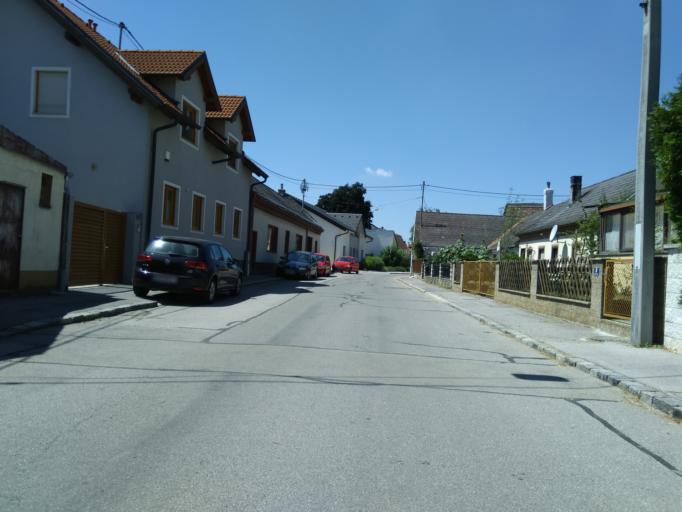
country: AT
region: Lower Austria
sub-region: Politischer Bezirk Mistelbach
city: Bockfliess
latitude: 48.3596
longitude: 16.5972
